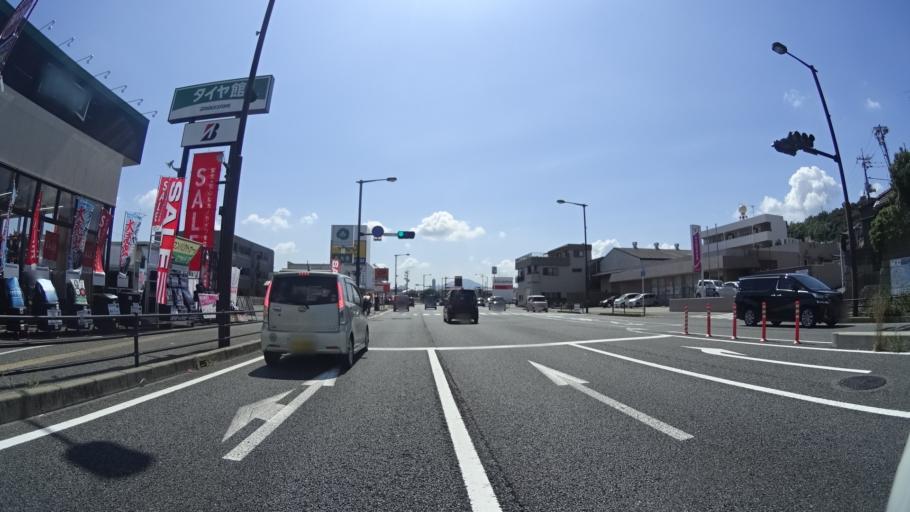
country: JP
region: Yamaguchi
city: Shimonoseki
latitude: 33.9728
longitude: 130.9194
